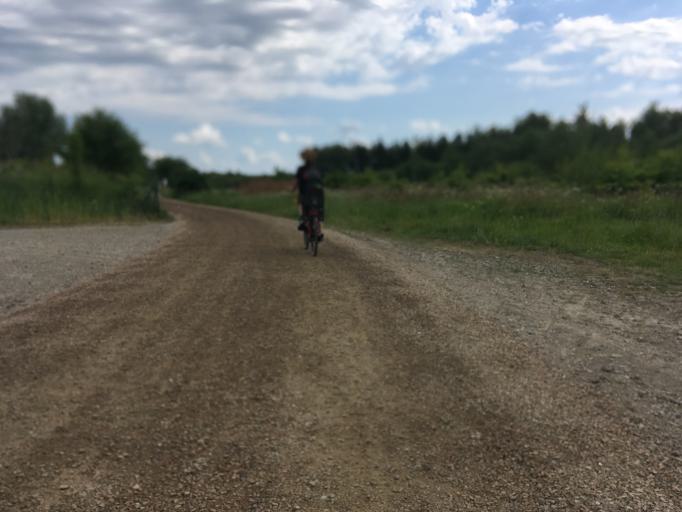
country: SE
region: Skane
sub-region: Staffanstorps Kommun
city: Hjaerup
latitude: 55.7020
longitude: 13.1481
